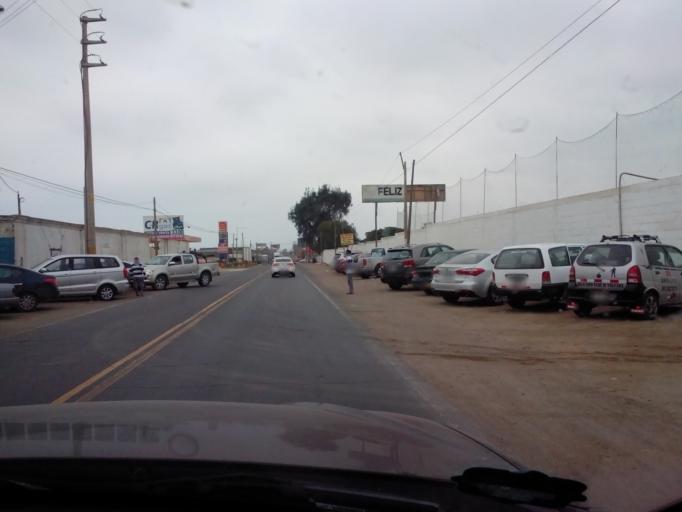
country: PE
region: Ica
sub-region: Provincia de Chincha
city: San Pedro
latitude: -13.4122
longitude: -76.1561
